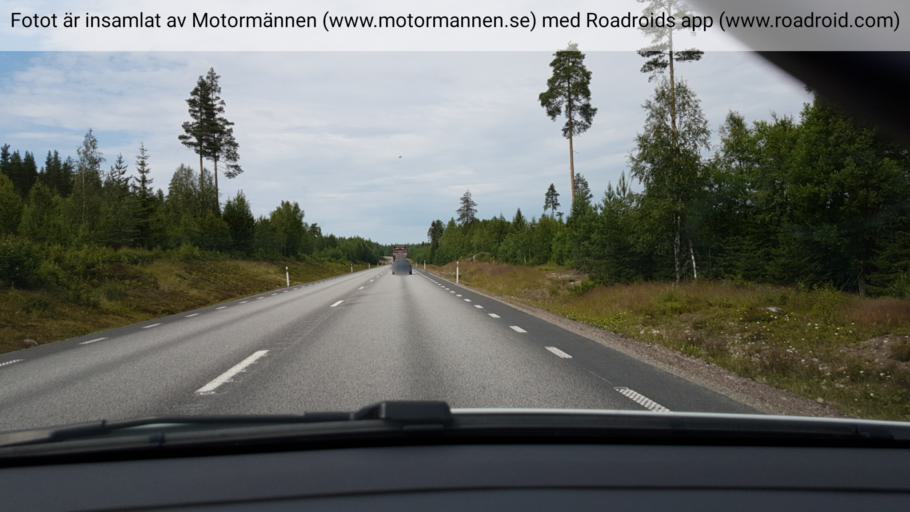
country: SE
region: Dalarna
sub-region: Rattviks Kommun
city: Raettvik
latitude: 60.8117
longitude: 15.2608
